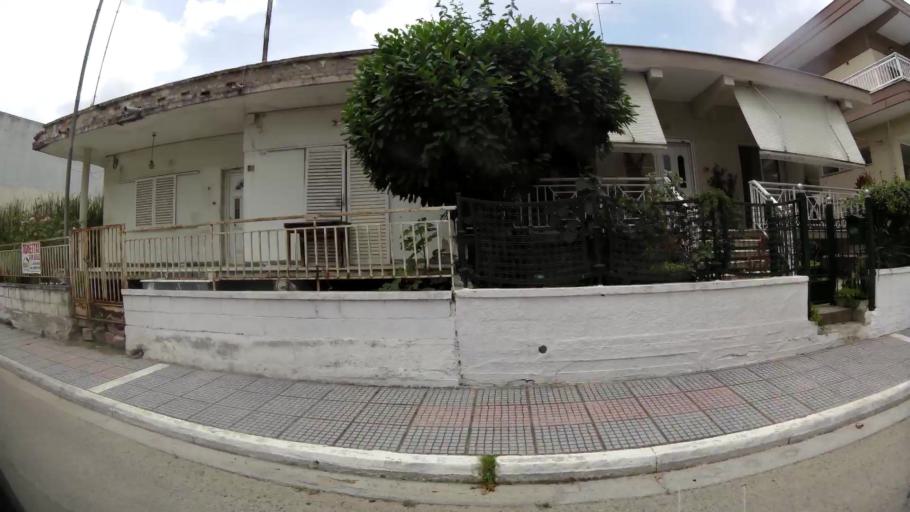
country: GR
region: Central Macedonia
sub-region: Nomos Pierias
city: Kallithea
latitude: 40.2749
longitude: 22.5764
